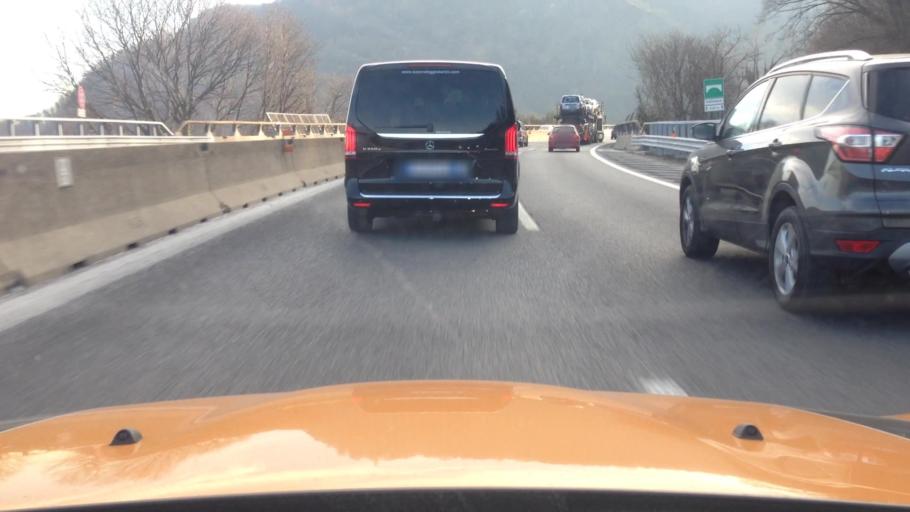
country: IT
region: Lombardy
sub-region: Provincia di Como
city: San Fermo della Battaglia
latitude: 45.8141
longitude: 9.0595
